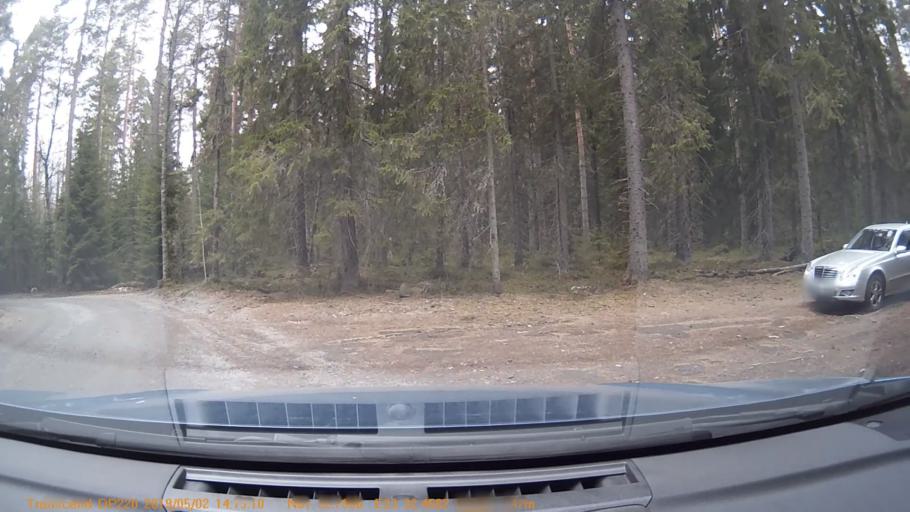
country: FI
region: Pirkanmaa
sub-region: Tampere
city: Yloejaervi
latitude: 61.5466
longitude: 23.5409
